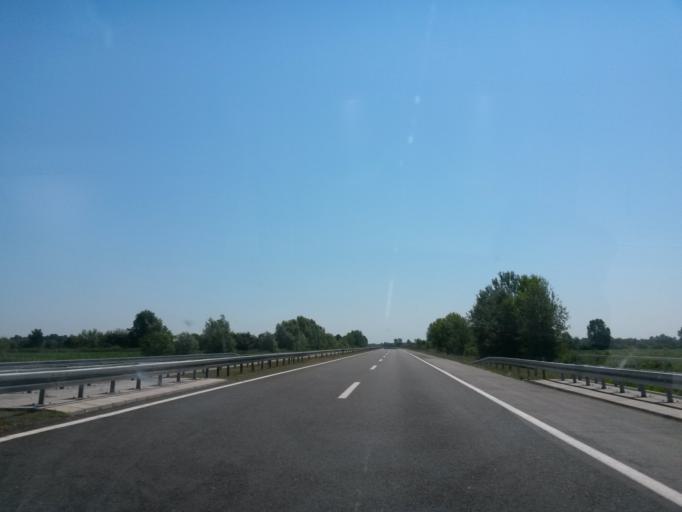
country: BA
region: Federation of Bosnia and Herzegovina
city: Donja Dubica
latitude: 45.1397
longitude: 18.3697
